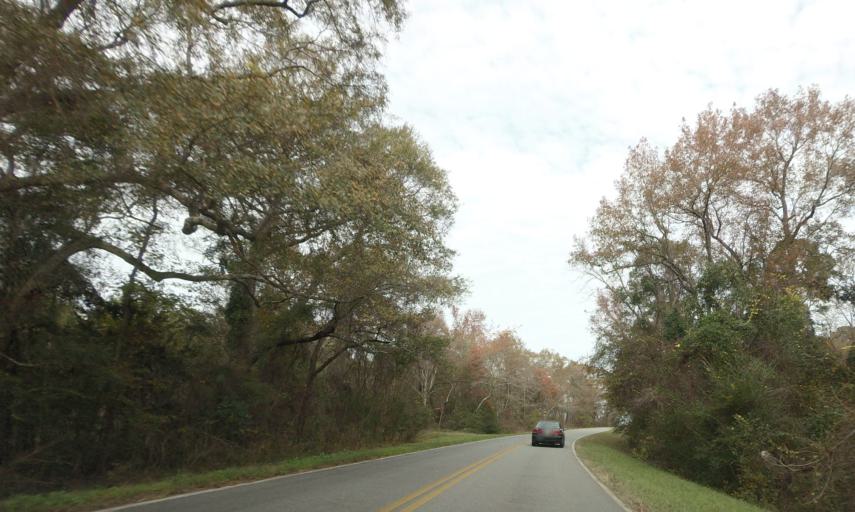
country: US
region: Georgia
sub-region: Dodge County
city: Chester
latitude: 32.4268
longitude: -83.1814
